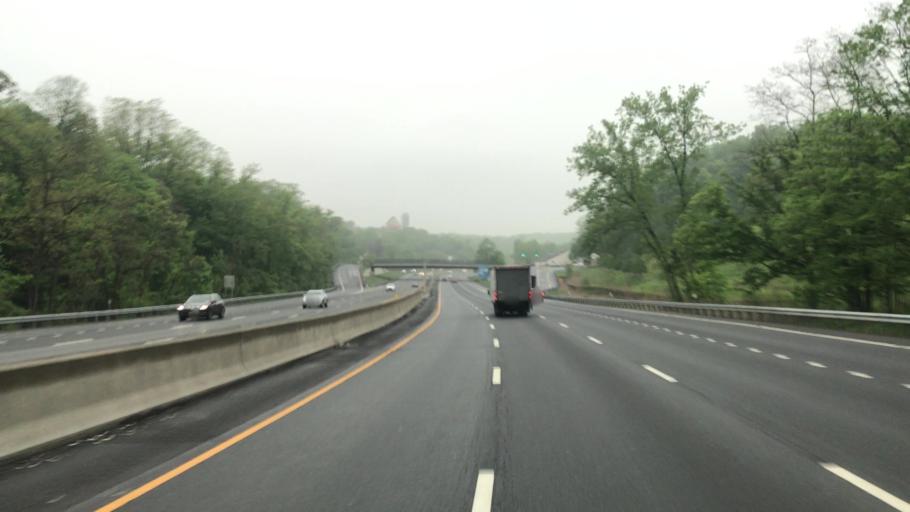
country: US
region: New York
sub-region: Westchester County
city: Tuckahoe
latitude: 40.9636
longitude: -73.8596
